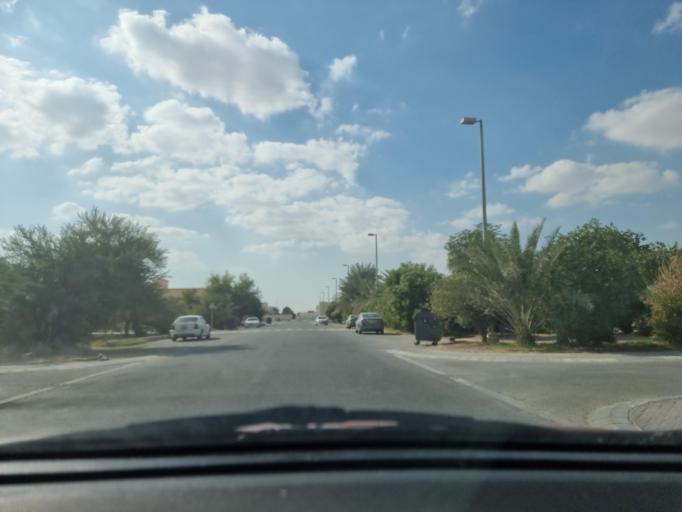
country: AE
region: Abu Dhabi
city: Abu Dhabi
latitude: 24.3833
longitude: 54.7040
